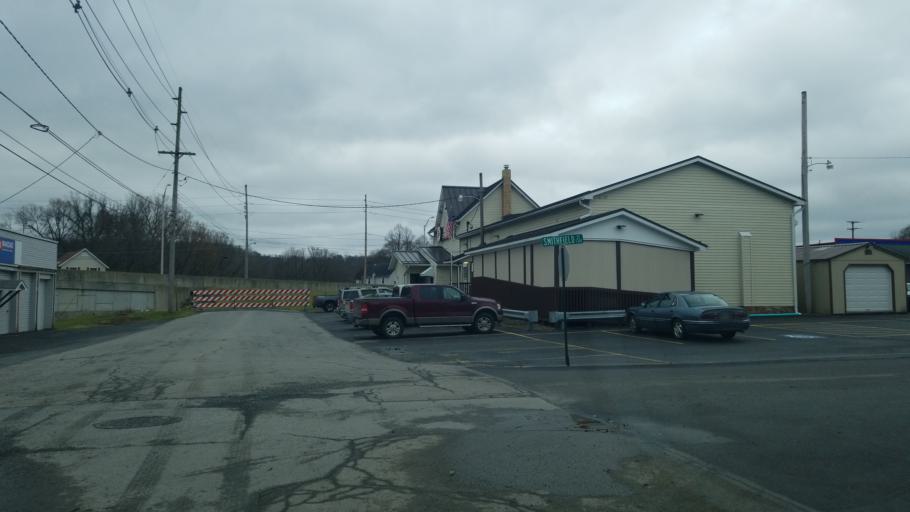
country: US
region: Pennsylvania
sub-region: Clearfield County
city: Sandy
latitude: 41.1112
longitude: -78.7709
